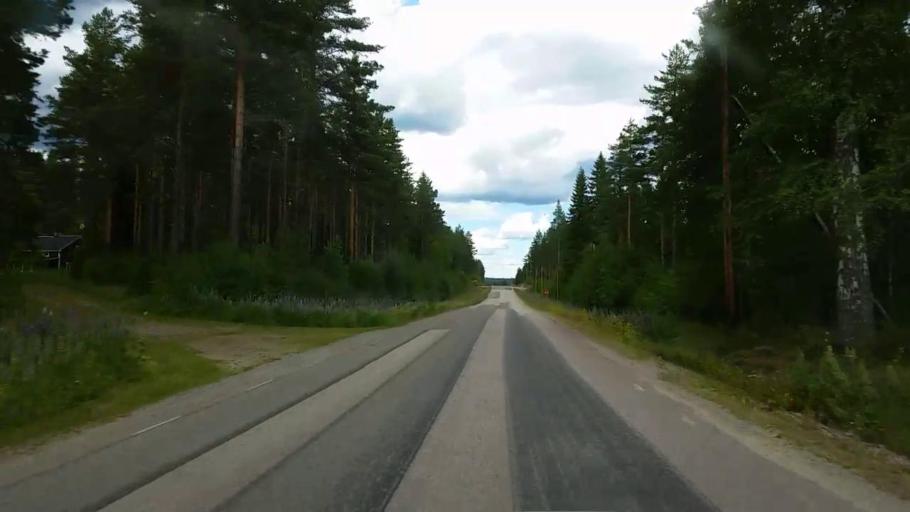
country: SE
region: Gaevleborg
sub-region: Ovanakers Kommun
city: Edsbyn
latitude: 61.4106
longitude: 15.8975
